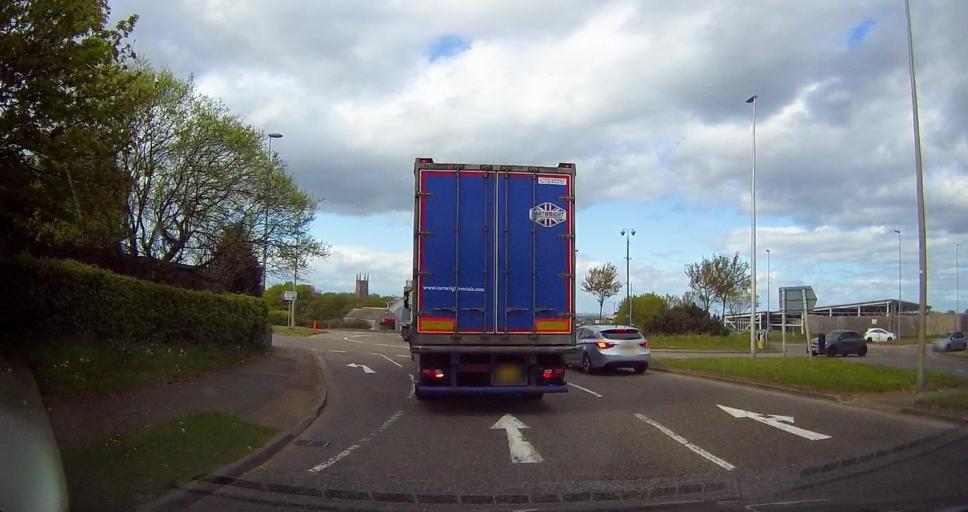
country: GB
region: Scotland
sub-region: Aberdeen City
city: Aberdeen
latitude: 57.1169
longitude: -2.0889
